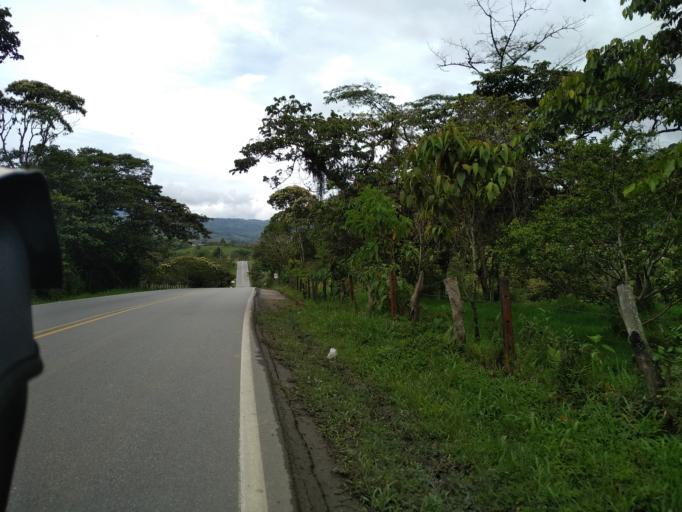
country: CO
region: Santander
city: Suaita
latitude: 6.1310
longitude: -73.3607
